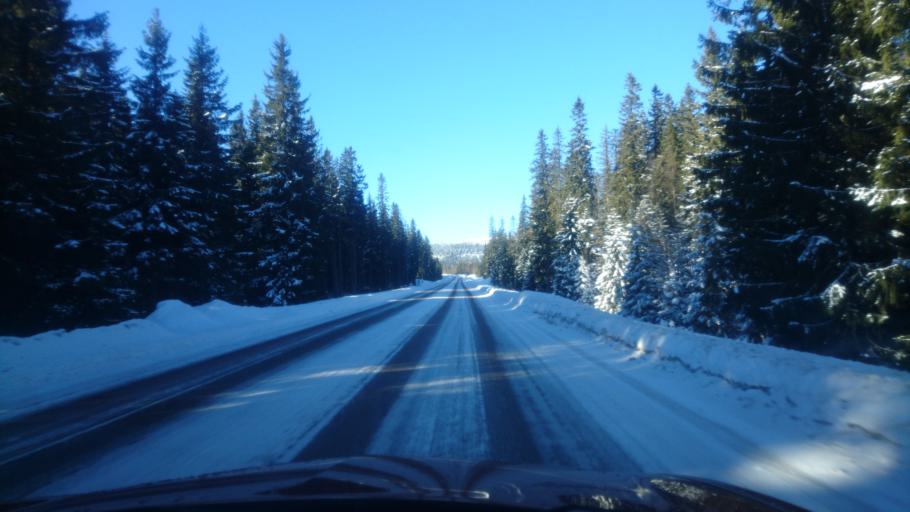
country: SE
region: Dalarna
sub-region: Malung-Saelens kommun
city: Malung
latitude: 61.1692
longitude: 13.1862
